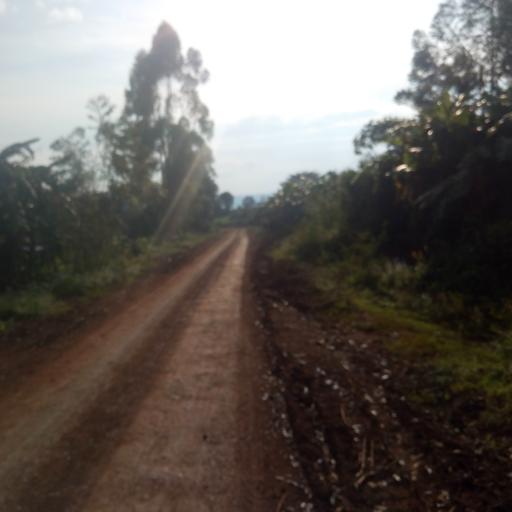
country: ET
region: Oromiya
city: Gore
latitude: 7.8976
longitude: 35.4928
